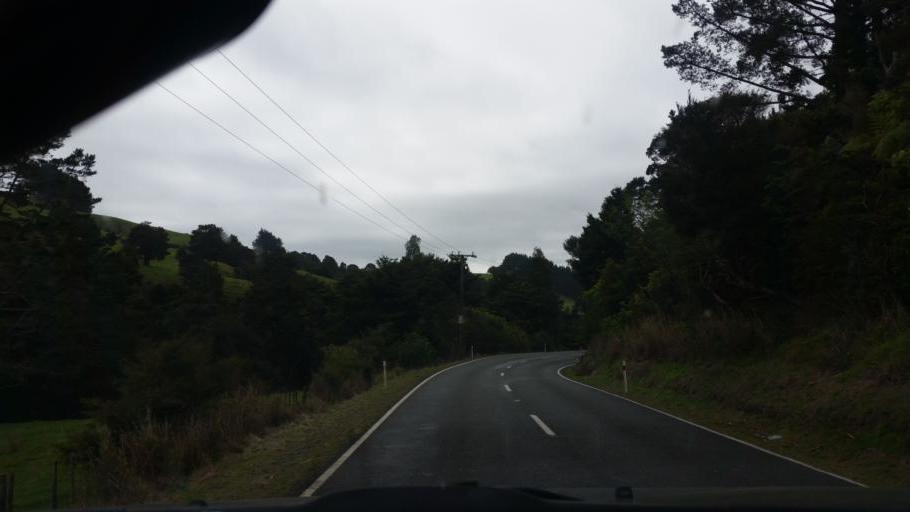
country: NZ
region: Northland
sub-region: Kaipara District
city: Dargaville
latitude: -35.8144
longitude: 173.7268
